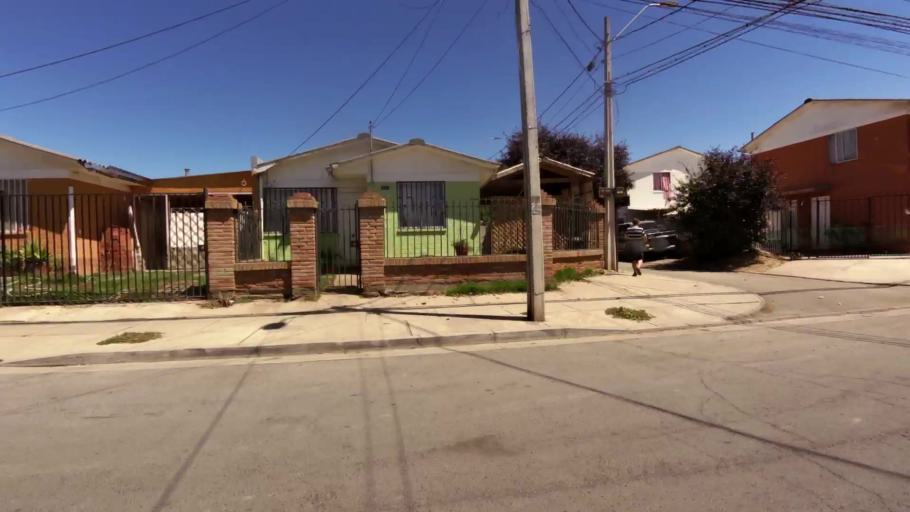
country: CL
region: O'Higgins
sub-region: Provincia de Cachapoal
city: Rancagua
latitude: -34.1667
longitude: -70.7816
